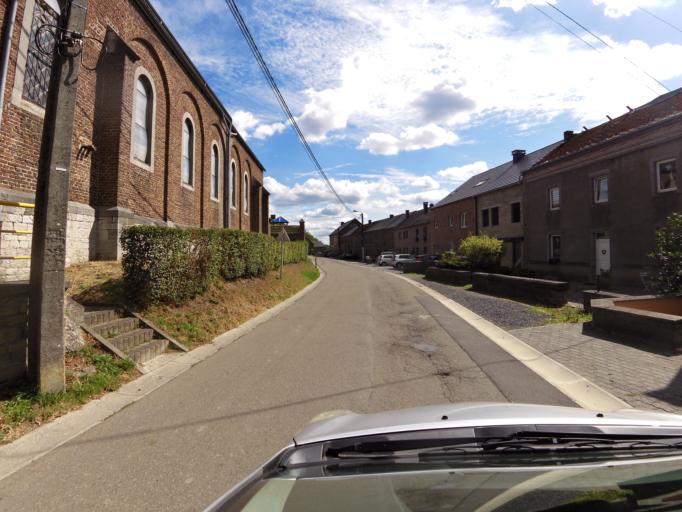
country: BE
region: Wallonia
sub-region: Province de Namur
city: Somme-Leuze
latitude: 50.3366
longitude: 5.3673
